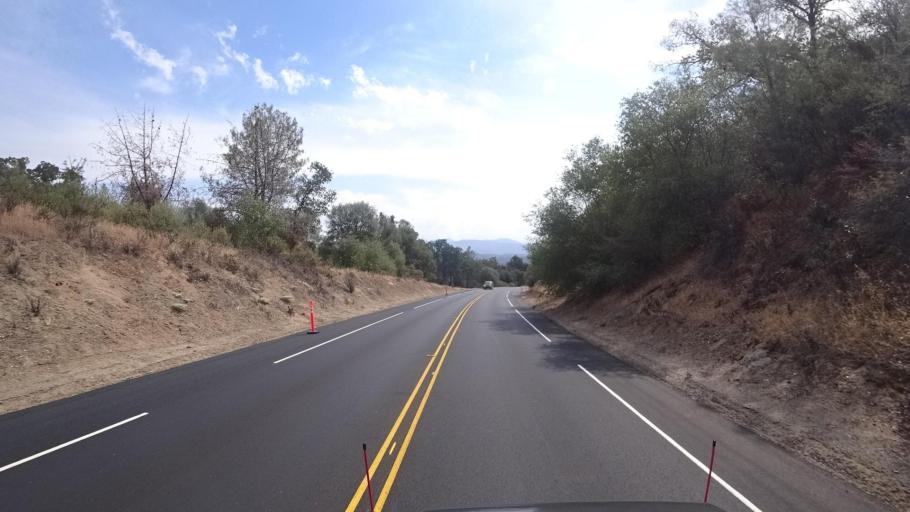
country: US
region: California
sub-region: Mariposa County
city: Mariposa
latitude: 37.4625
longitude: -119.8977
